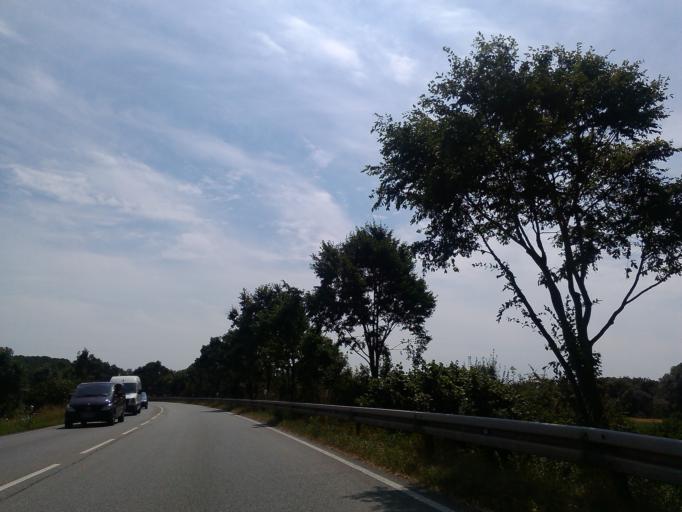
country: DE
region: Bavaria
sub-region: Upper Bavaria
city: Emmering
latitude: 48.1980
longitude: 11.3025
